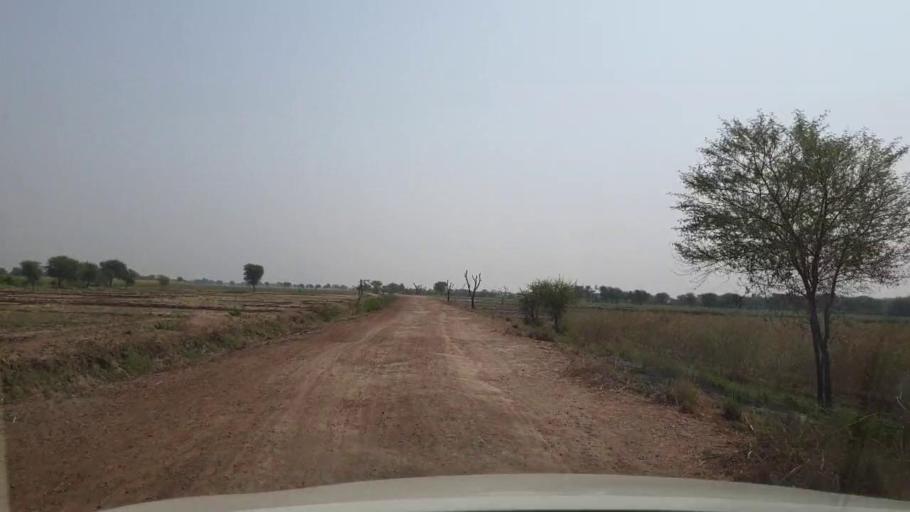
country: PK
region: Sindh
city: Dhoro Naro
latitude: 25.4608
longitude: 69.6651
